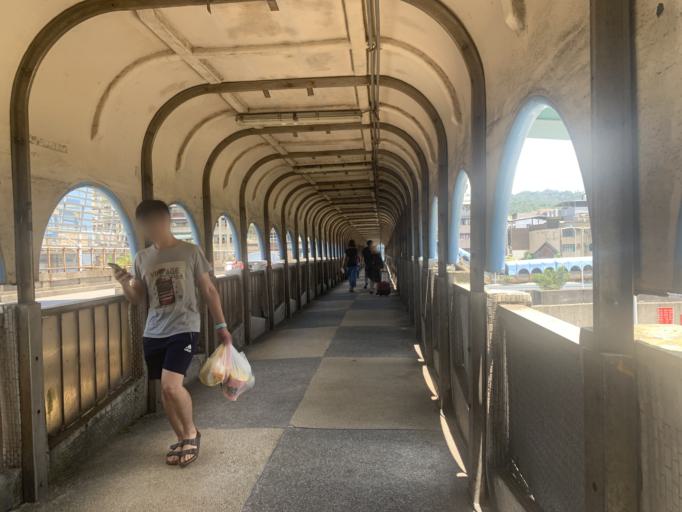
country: TW
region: Taiwan
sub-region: Keelung
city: Keelung
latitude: 25.1313
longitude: 121.7376
